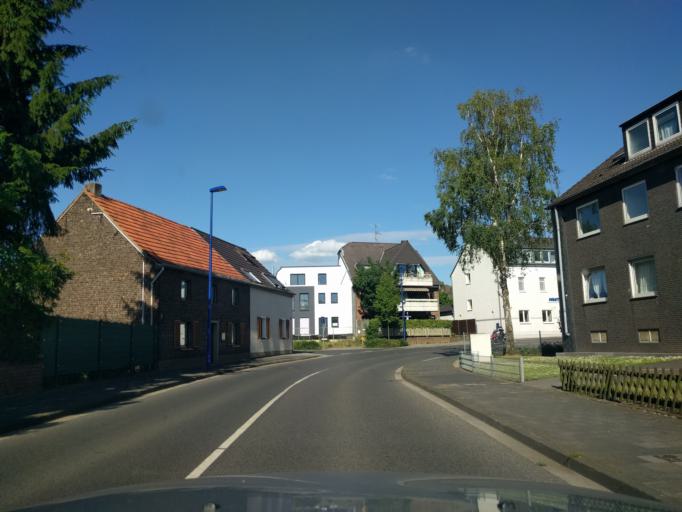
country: DE
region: North Rhine-Westphalia
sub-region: Regierungsbezirk Dusseldorf
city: Meerbusch
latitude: 51.2508
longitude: 6.6814
